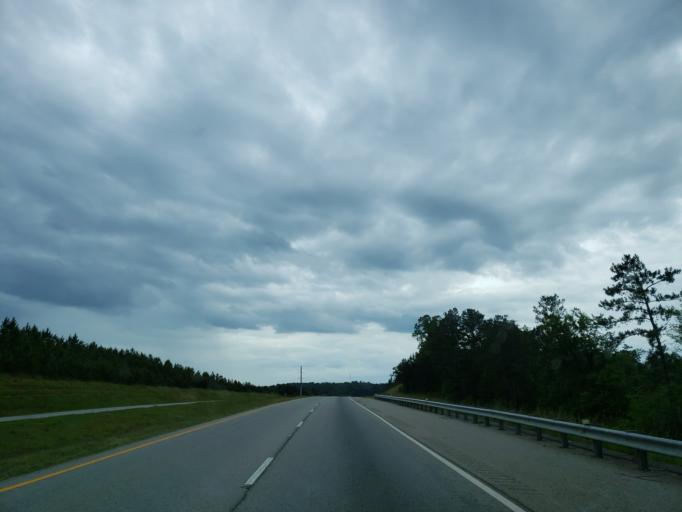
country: US
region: Georgia
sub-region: Polk County
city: Cedartown
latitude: 34.0114
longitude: -85.2211
